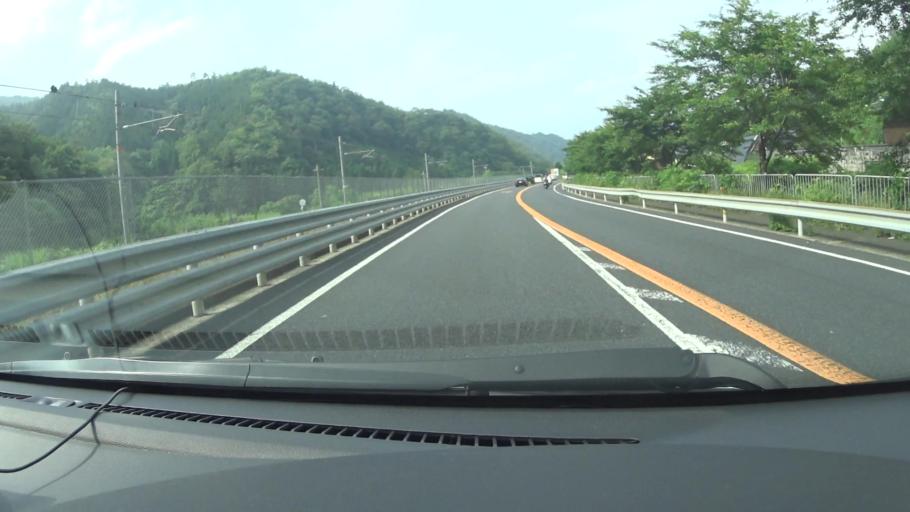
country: JP
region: Kyoto
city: Maizuru
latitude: 35.3993
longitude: 135.3200
